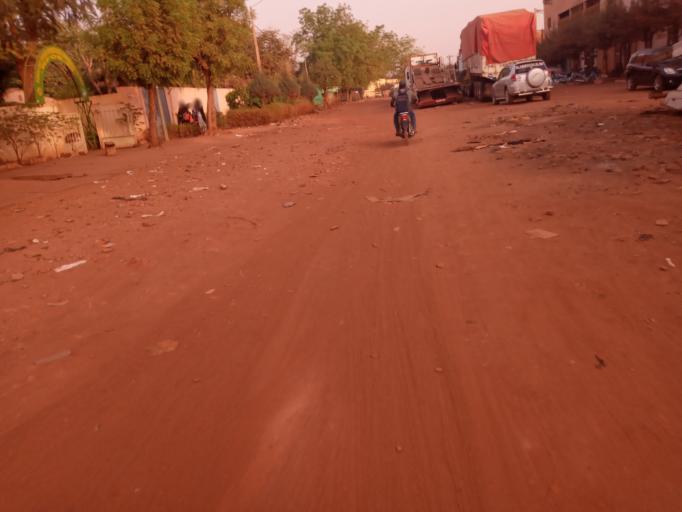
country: ML
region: Bamako
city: Bamako
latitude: 12.5937
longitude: -7.9599
